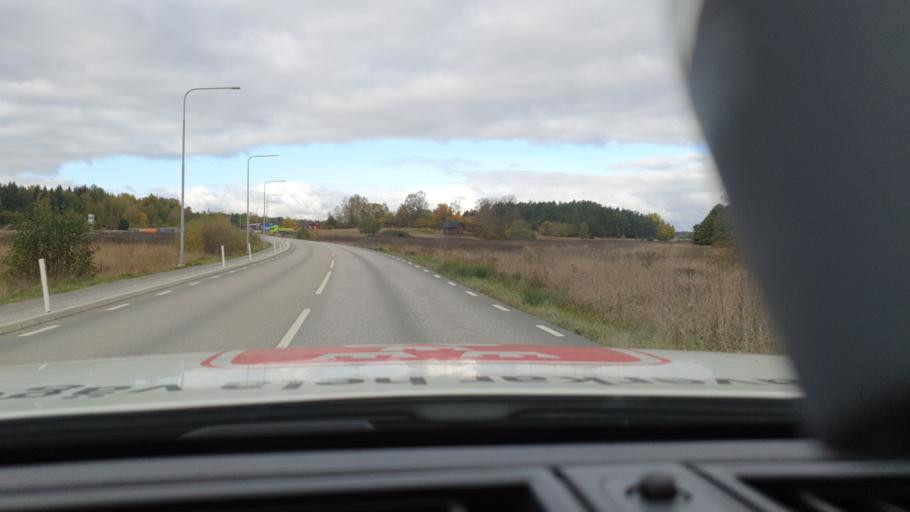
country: SE
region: Stockholm
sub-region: Upplands-Bro Kommun
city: Bro
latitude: 59.5124
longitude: 17.6222
